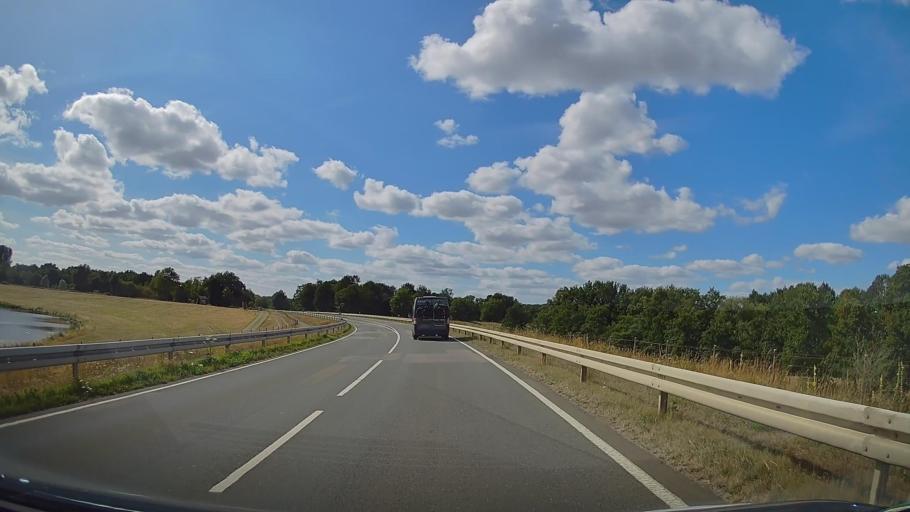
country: DE
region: Lower Saxony
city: Alfhausen
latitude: 52.4982
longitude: 7.9807
